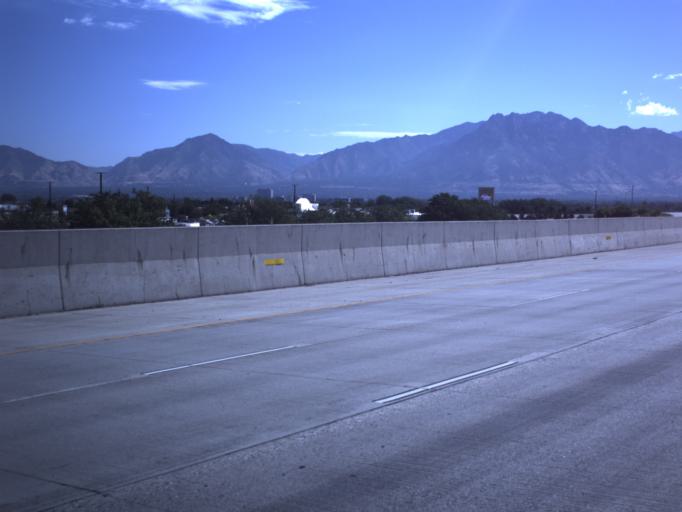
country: US
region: Utah
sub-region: Salt Lake County
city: Taylorsville
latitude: 40.6452
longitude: -111.9452
